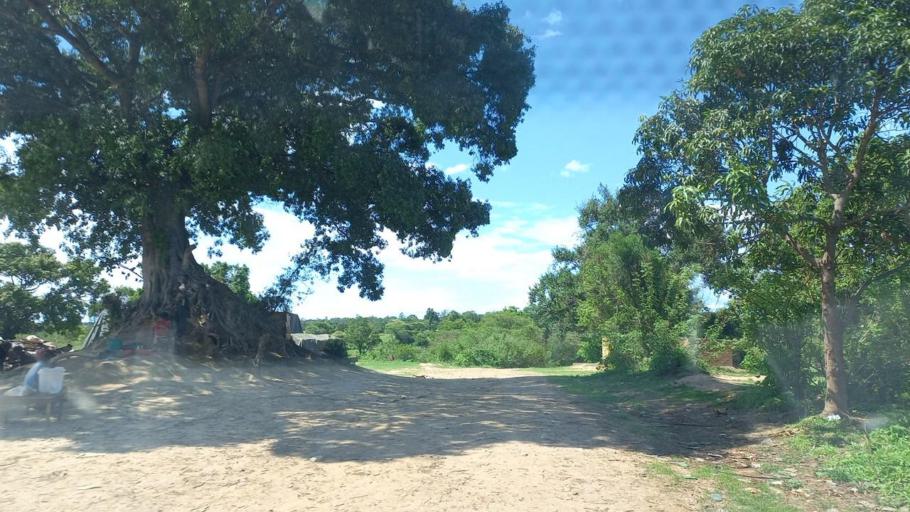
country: ZM
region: North-Western
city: Kabompo
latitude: -13.6165
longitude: 24.2094
